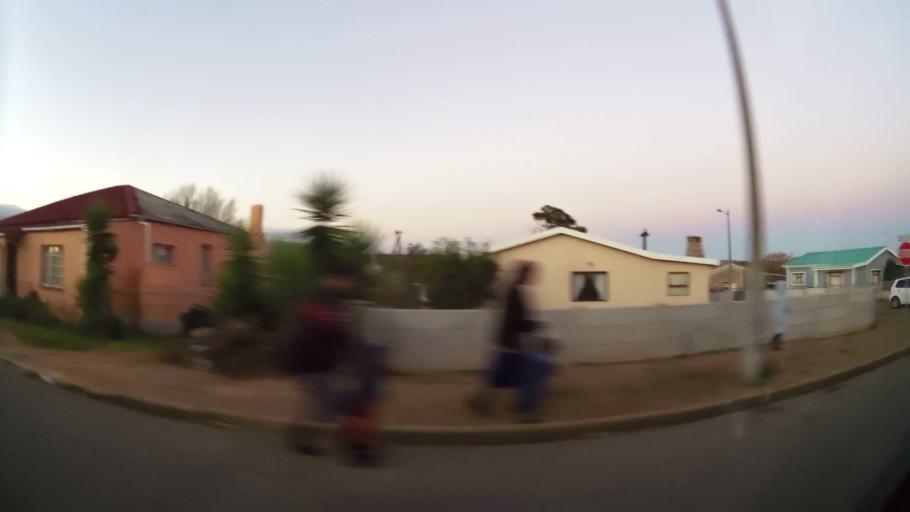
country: ZA
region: Western Cape
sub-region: Eden District Municipality
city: Riversdale
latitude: -34.0998
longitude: 21.2678
